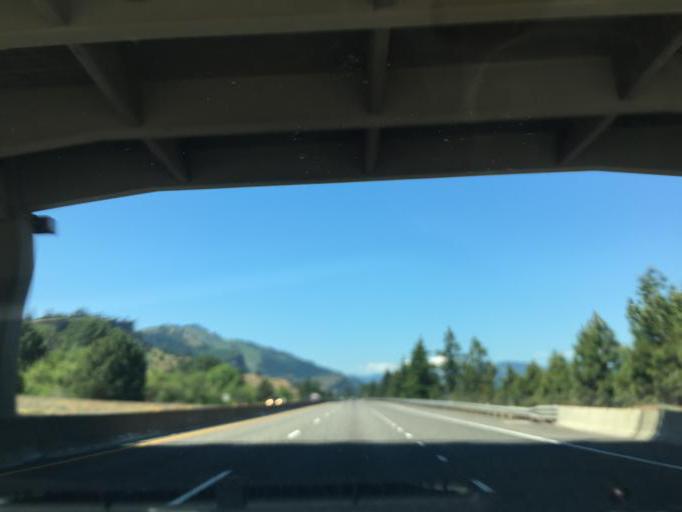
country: US
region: Washington
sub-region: Klickitat County
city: White Salmon
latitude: 45.6861
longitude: -121.4009
